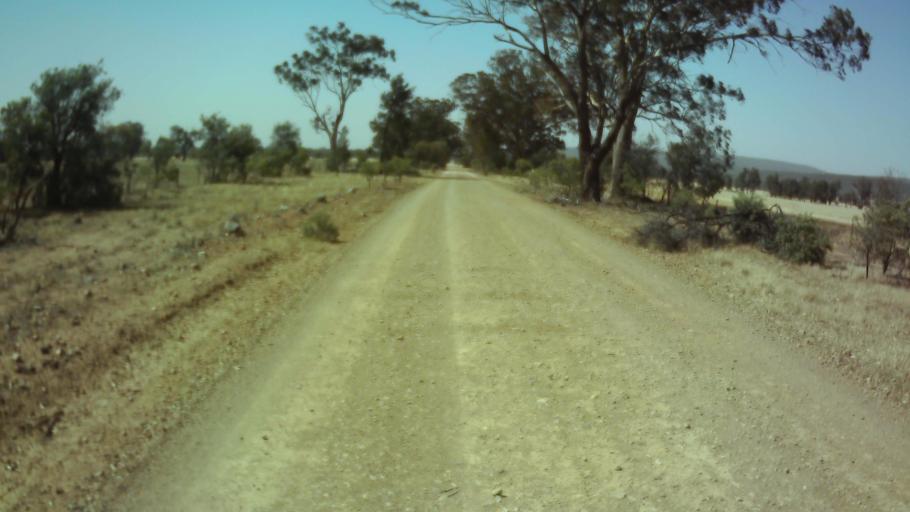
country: AU
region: New South Wales
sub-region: Weddin
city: Grenfell
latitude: -33.9912
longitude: 147.9264
